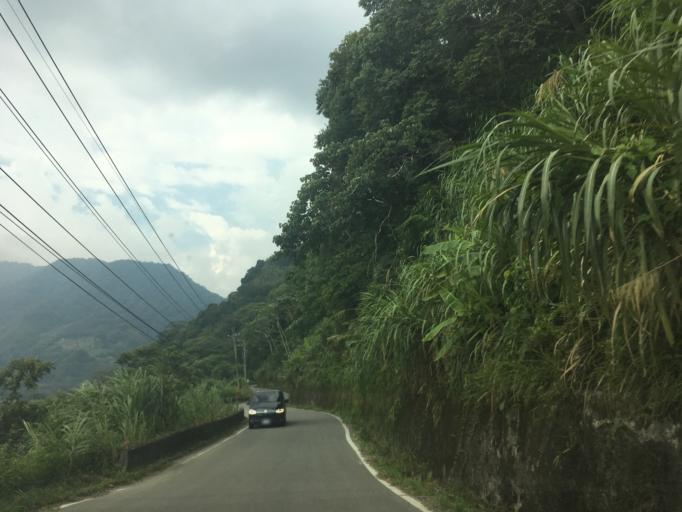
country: TW
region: Taiwan
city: Fengyuan
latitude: 24.3470
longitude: 120.9440
